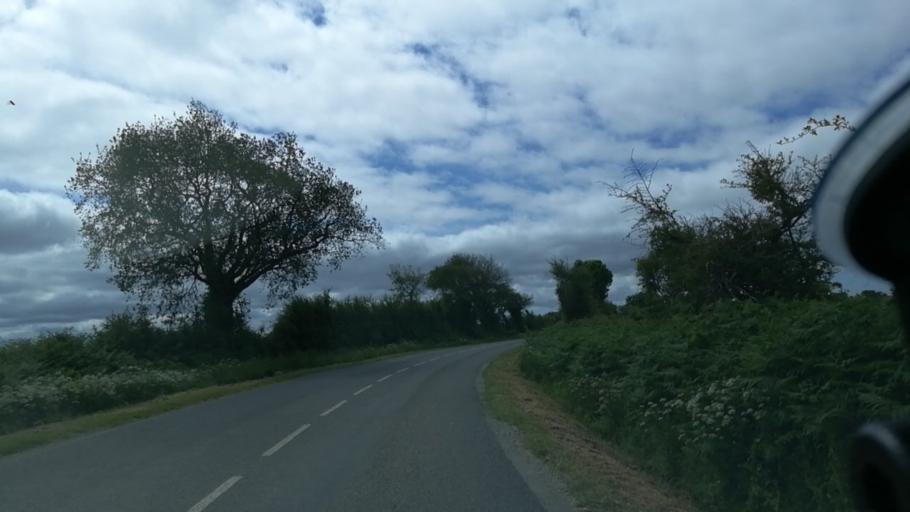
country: FR
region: Brittany
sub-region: Departement du Morbihan
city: Penestin
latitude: 47.4711
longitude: -2.4313
